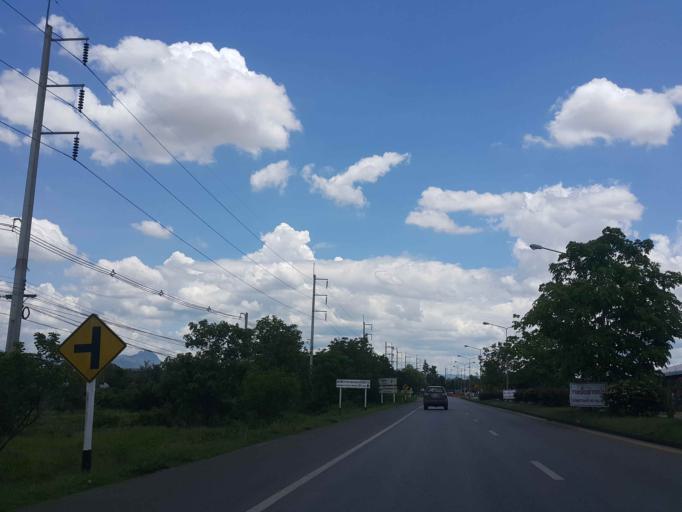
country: TH
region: Phrae
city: Nong Muang Khai
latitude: 18.2130
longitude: 100.1989
